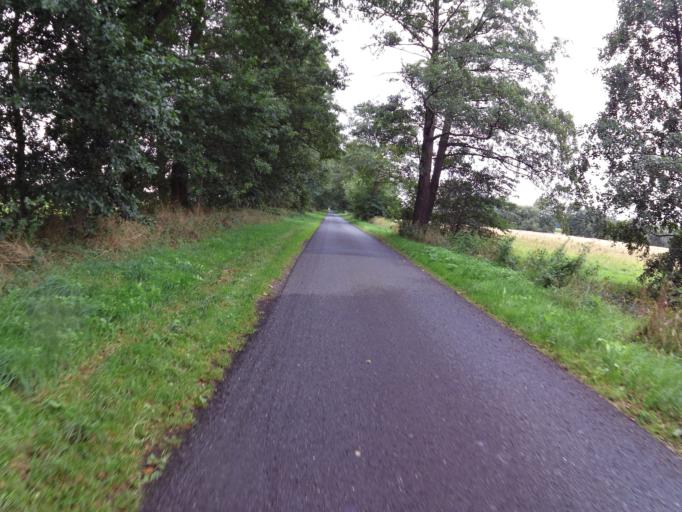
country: DE
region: Lower Saxony
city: Scheessel
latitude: 53.1610
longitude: 9.4595
